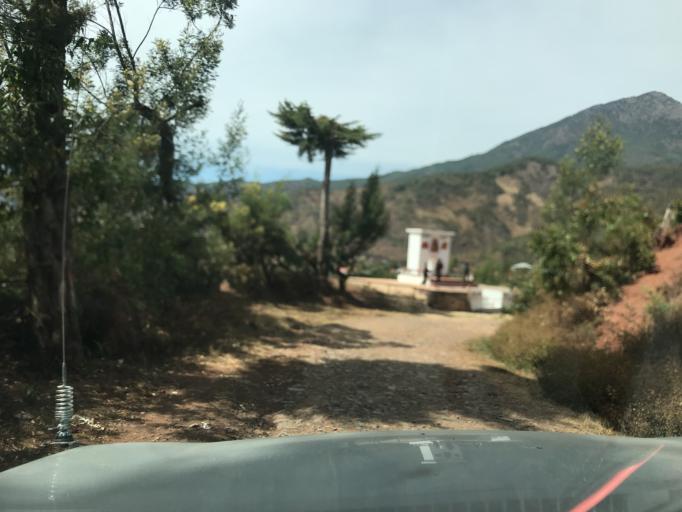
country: TL
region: Ainaro
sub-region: Ainaro
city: Ainaro
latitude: -8.8858
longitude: 125.5218
